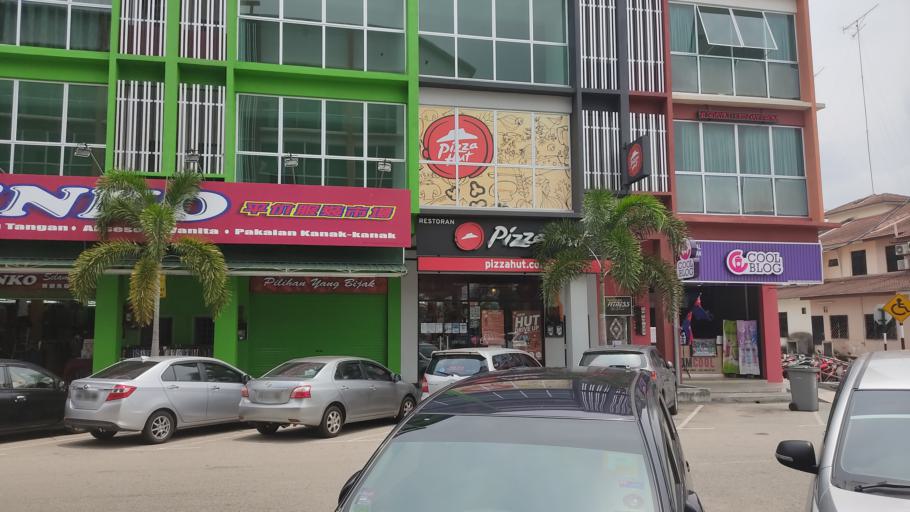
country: MY
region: Johor
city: Tangkak
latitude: 2.2740
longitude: 102.5432
